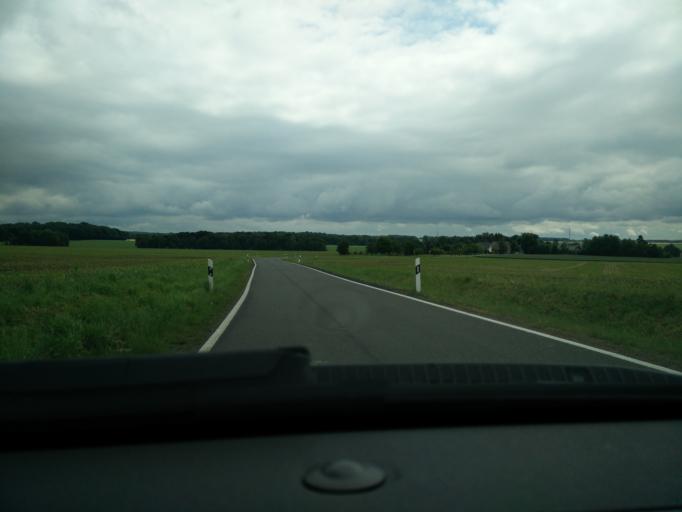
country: DE
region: Saxony
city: Bad Lausick
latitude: 51.1097
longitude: 12.6624
